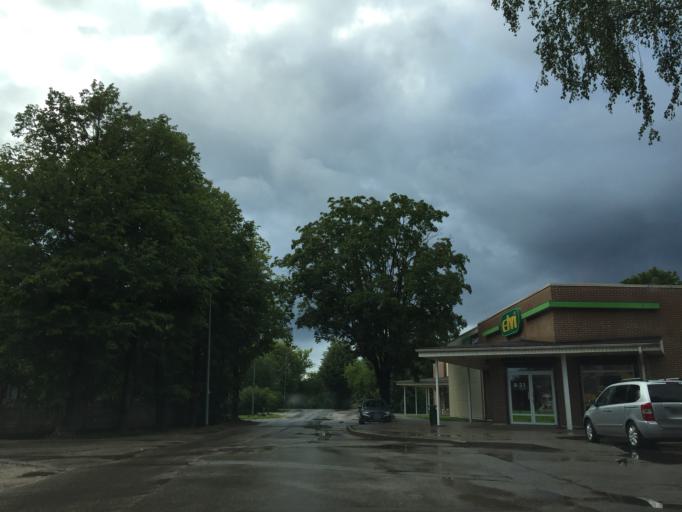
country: LV
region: Babite
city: Pinki
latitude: 56.9561
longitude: 23.9486
